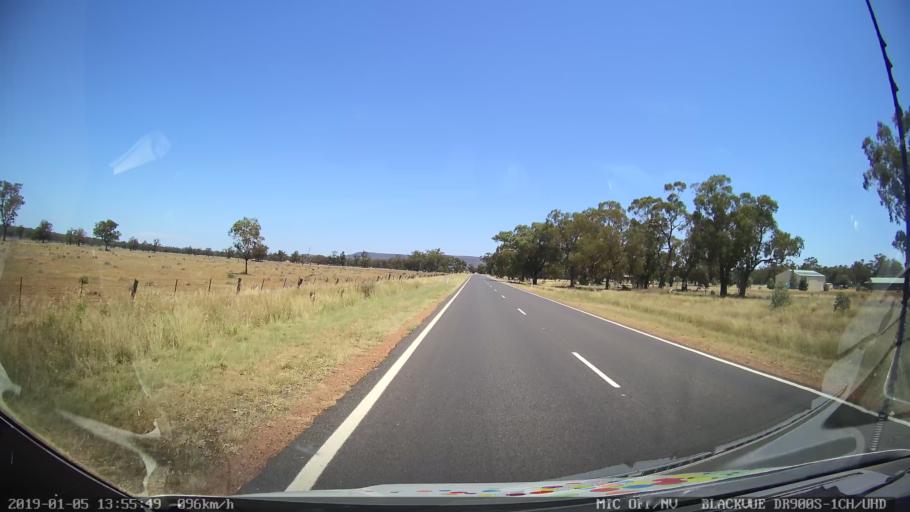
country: AU
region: New South Wales
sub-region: Gunnedah
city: Gunnedah
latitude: -31.1084
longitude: 150.2698
